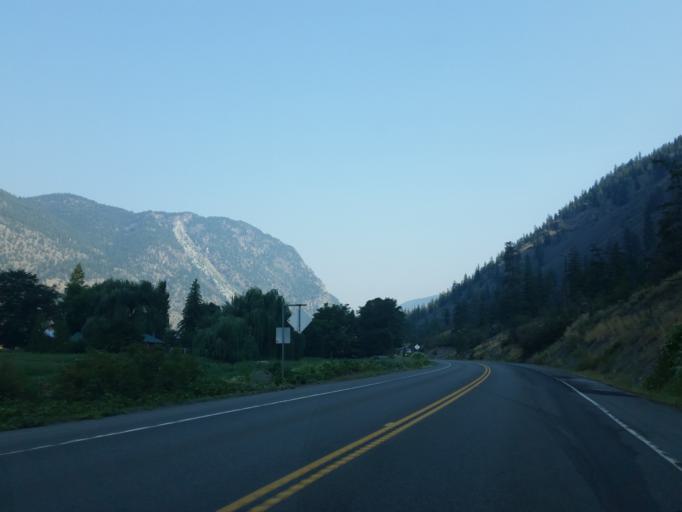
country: CA
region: British Columbia
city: Oliver
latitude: 49.2688
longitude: -120.0192
